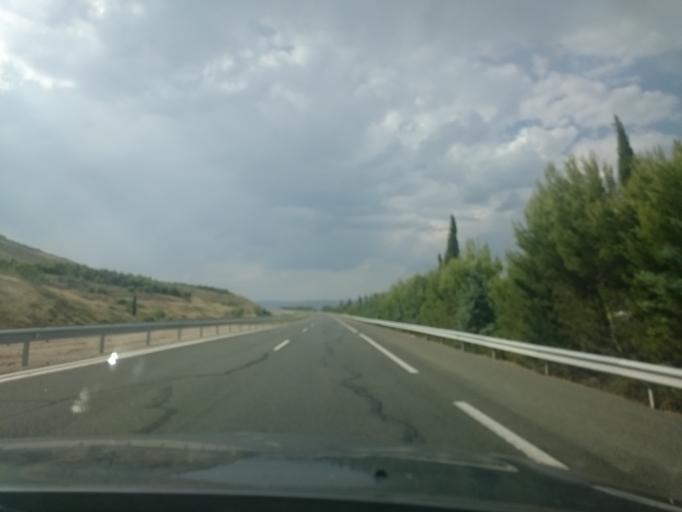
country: ES
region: La Rioja
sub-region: Provincia de La Rioja
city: Arrubal
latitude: 42.4174
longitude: -2.2623
